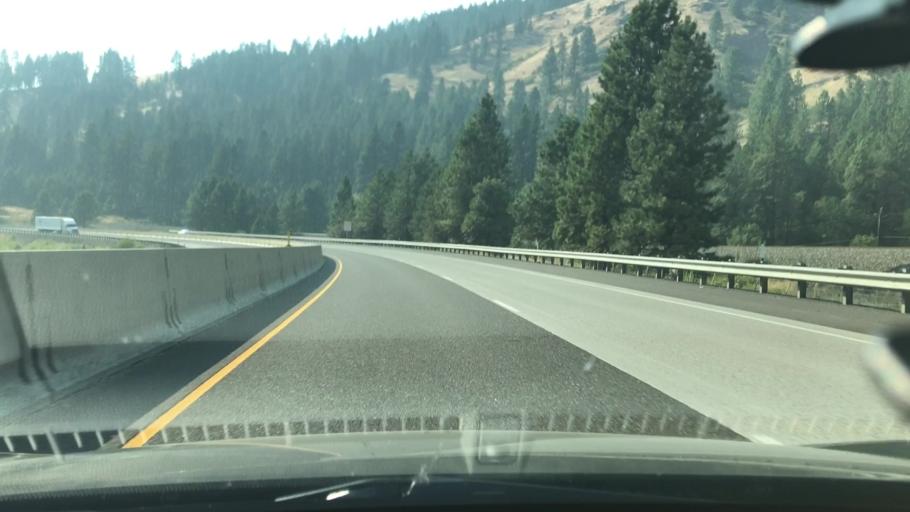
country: US
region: Oregon
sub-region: Union County
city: La Grande
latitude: 45.3543
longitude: -118.1862
